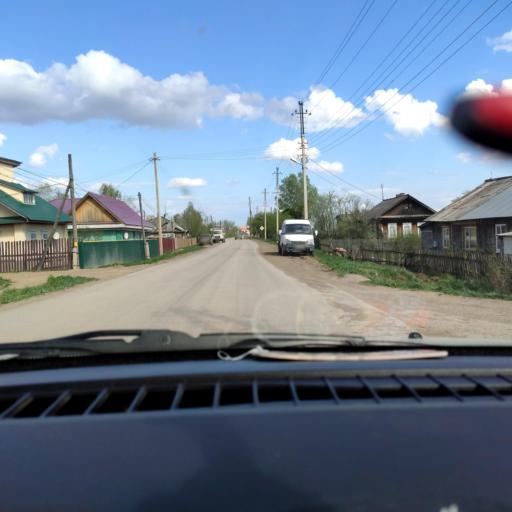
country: RU
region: Perm
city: Kudymkar
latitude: 59.0072
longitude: 54.6701
